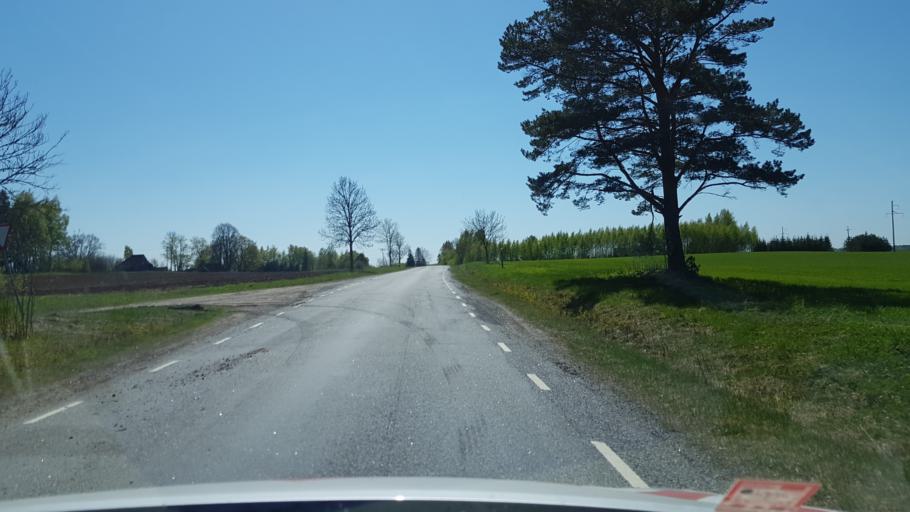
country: EE
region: Vorumaa
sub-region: Voru linn
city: Voru
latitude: 57.9305
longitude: 26.9516
